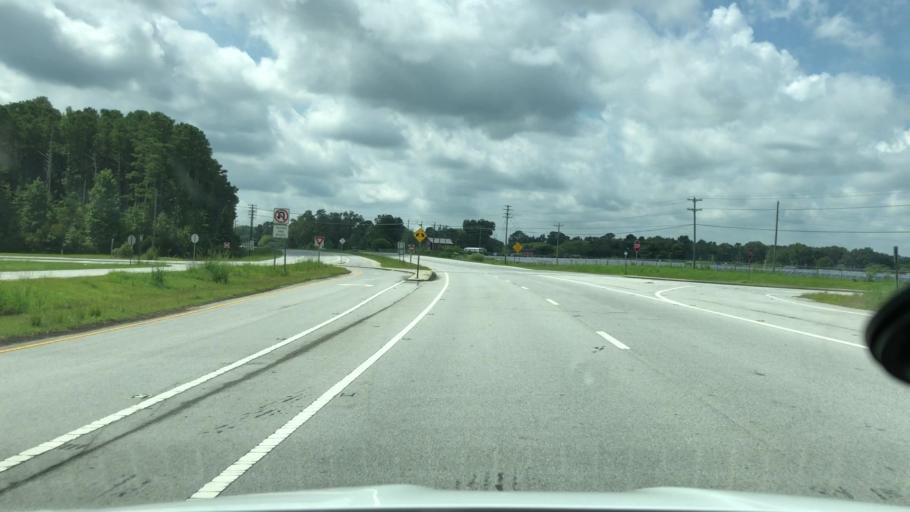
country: US
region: North Carolina
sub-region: Beaufort County
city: Washington
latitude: 35.5010
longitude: -77.1026
